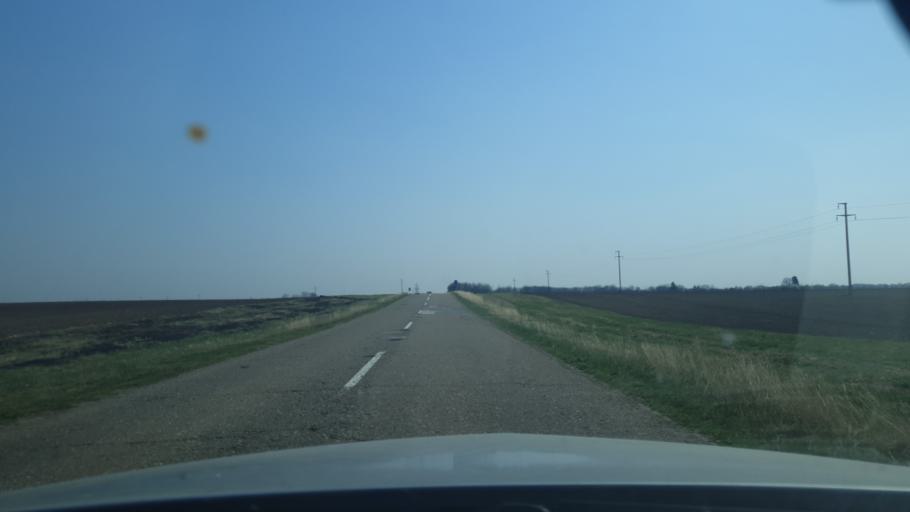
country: RS
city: Sasinci
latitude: 45.0261
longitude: 19.7597
